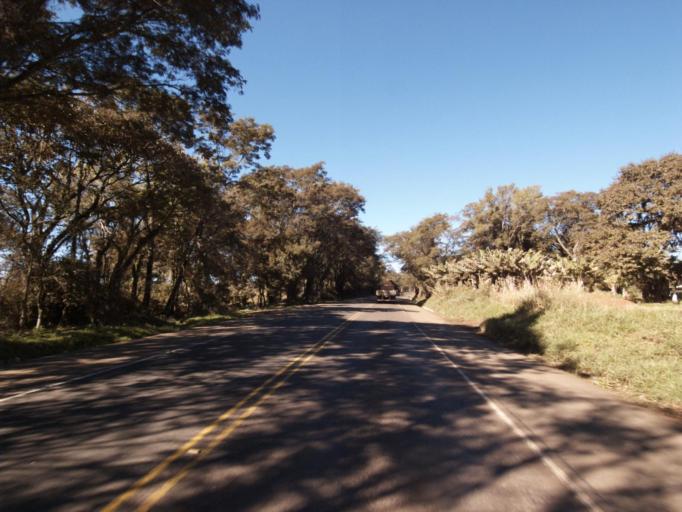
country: BR
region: Santa Catarina
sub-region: Chapeco
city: Chapeco
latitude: -26.9612
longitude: -52.7647
